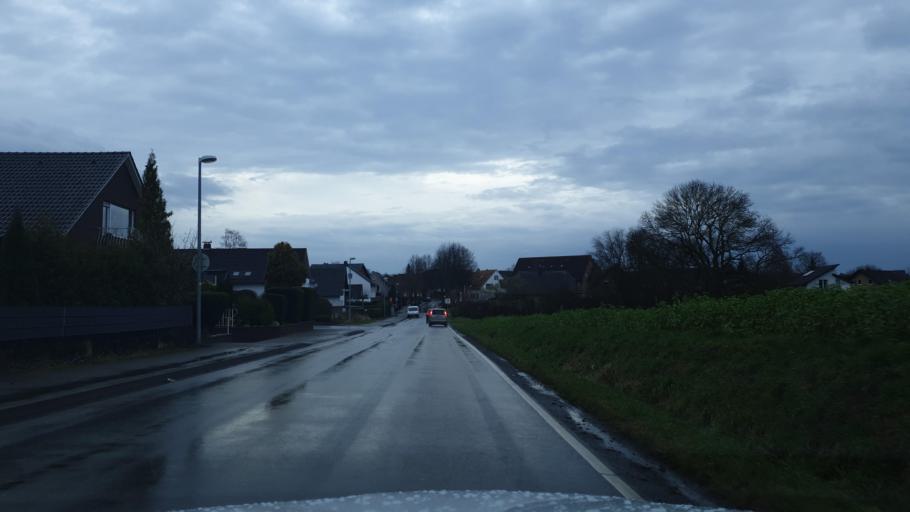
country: DE
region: North Rhine-Westphalia
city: Bad Oeynhausen
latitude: 52.1975
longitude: 8.8369
